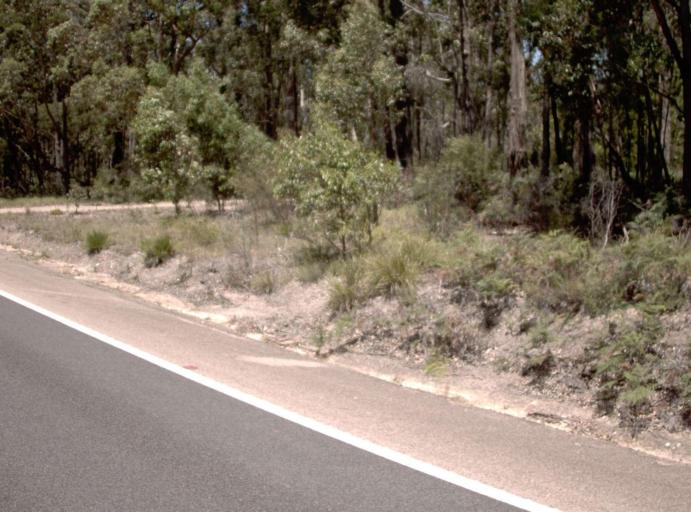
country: AU
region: Victoria
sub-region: East Gippsland
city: Lakes Entrance
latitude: -37.7533
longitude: 148.3473
